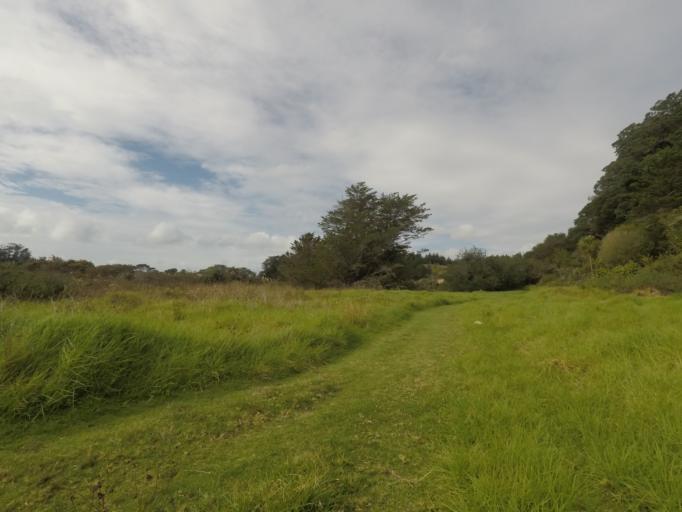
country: NZ
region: Auckland
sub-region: Auckland
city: Rothesay Bay
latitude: -36.6418
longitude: 174.7222
